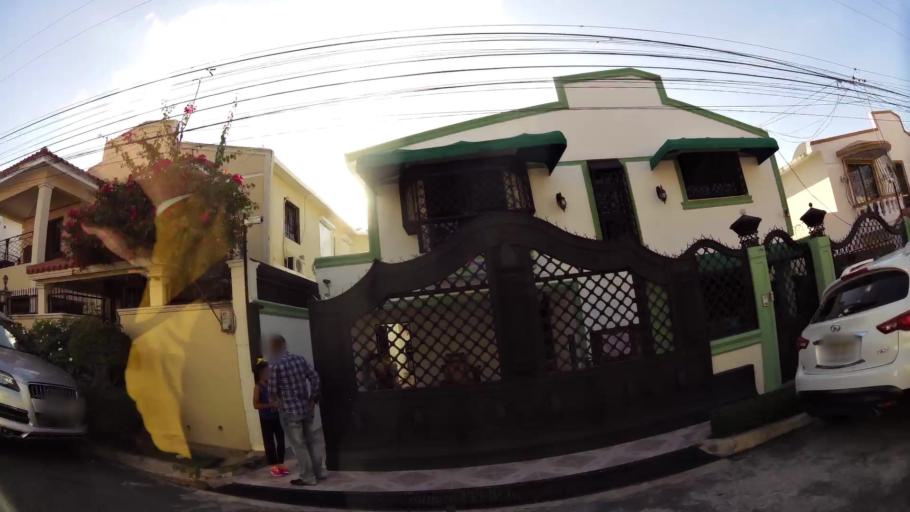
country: DO
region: Nacional
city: Santo Domingo
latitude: 18.4981
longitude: -69.9672
